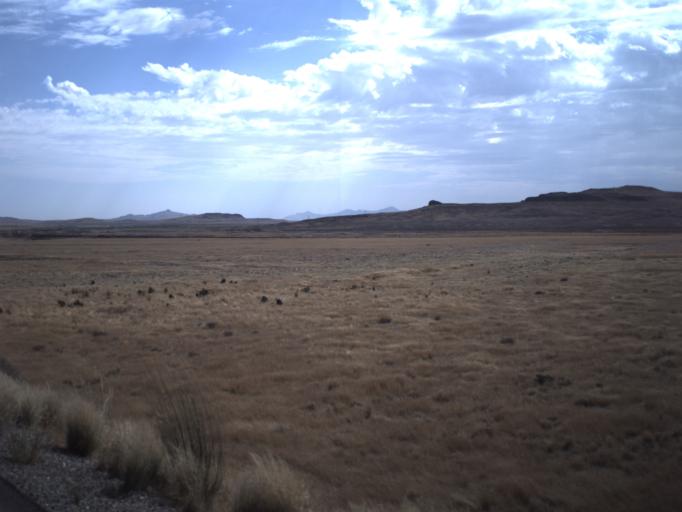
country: US
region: Utah
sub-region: Tooele County
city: Wendover
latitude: 41.3767
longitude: -114.0084
